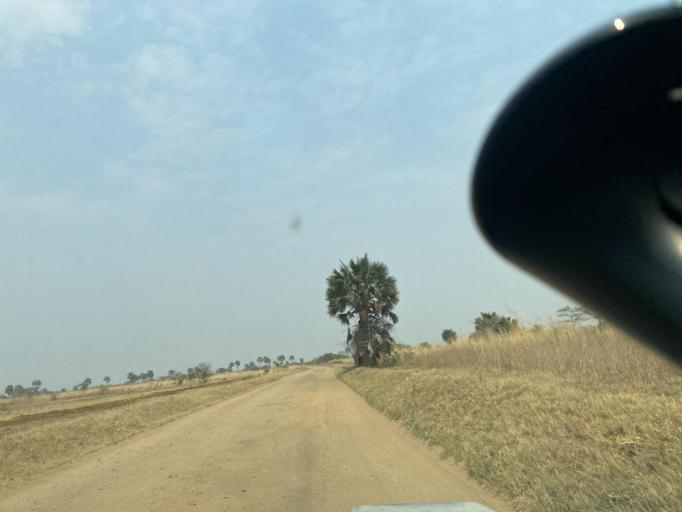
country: ZM
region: Lusaka
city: Kafue
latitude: -15.6483
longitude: 28.0700
